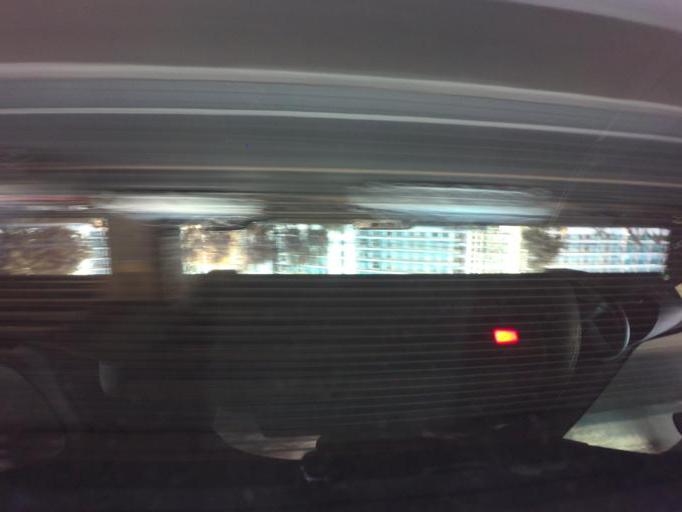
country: PH
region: Calabarzon
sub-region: Province of Rizal
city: Taguig
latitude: 14.4837
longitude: 121.0453
